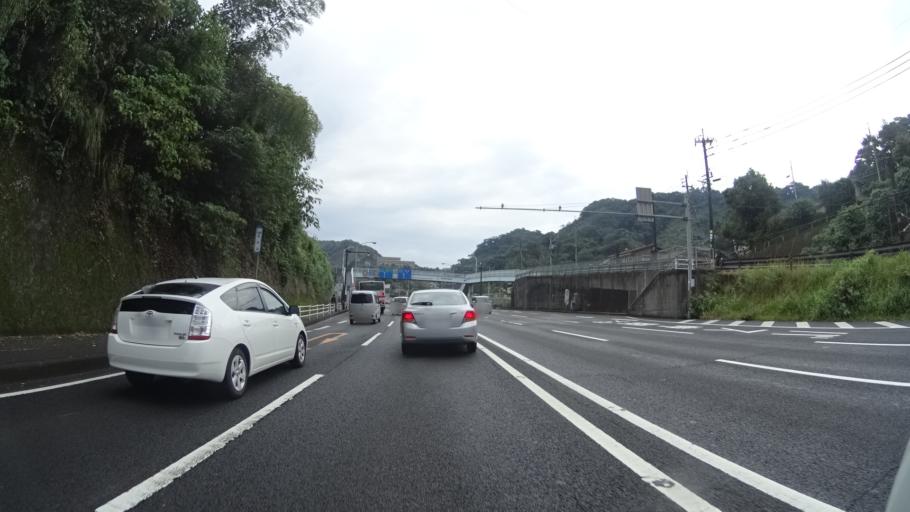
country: JP
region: Kagoshima
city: Kagoshima-shi
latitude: 31.6099
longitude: 130.5697
